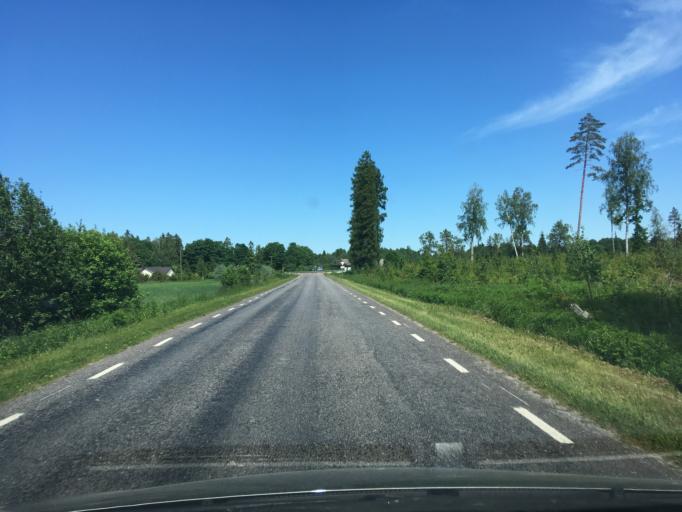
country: EE
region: Raplamaa
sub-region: Rapla vald
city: Rapla
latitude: 59.0661
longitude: 24.9133
